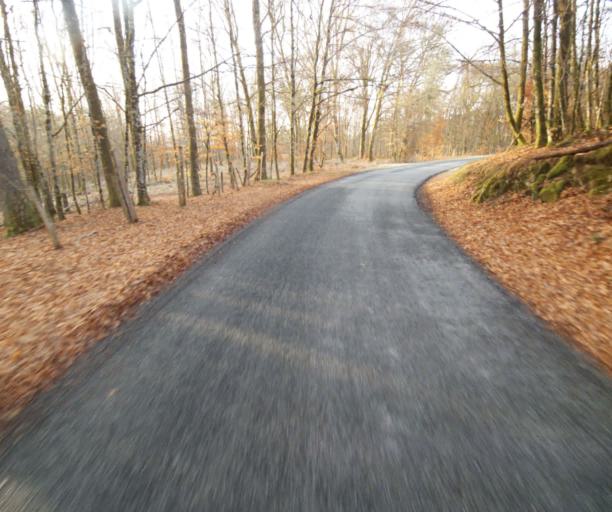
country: FR
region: Limousin
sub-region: Departement de la Correze
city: Correze
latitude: 45.3168
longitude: 1.8603
